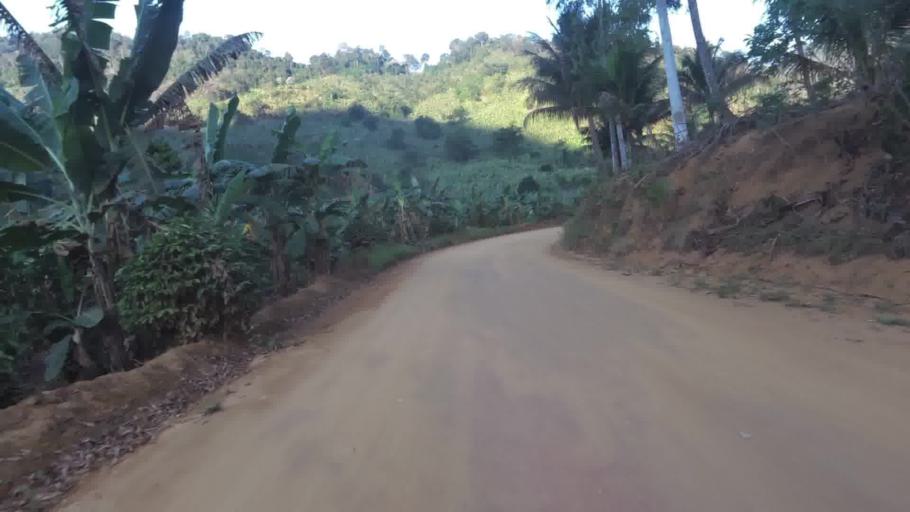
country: BR
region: Espirito Santo
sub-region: Alfredo Chaves
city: Alfredo Chaves
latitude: -20.5901
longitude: -40.7003
